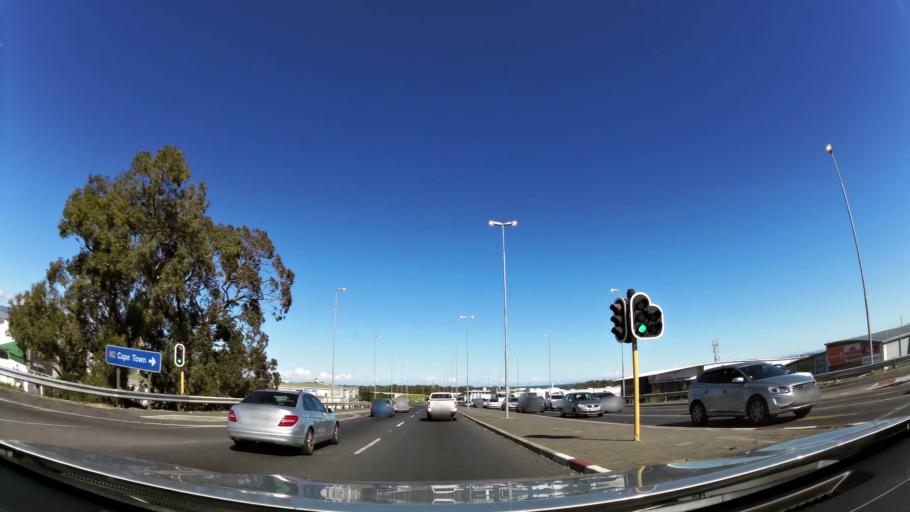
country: ZA
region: Western Cape
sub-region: Cape Winelands District Municipality
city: Stellenbosch
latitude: -34.0777
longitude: 18.8206
